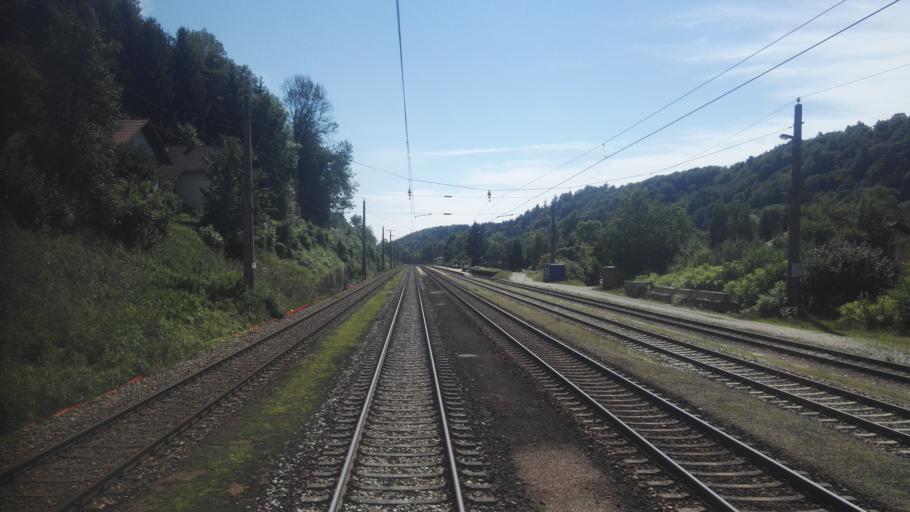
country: AT
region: Upper Austria
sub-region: Politischer Bezirk Scharding
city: Scharding
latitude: 48.5058
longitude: 13.4572
